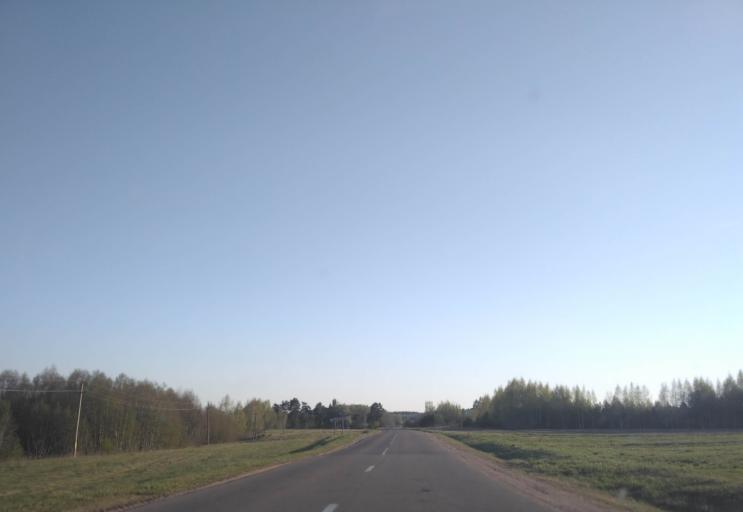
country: BY
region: Minsk
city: Radashkovichy
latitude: 54.1469
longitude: 27.2145
